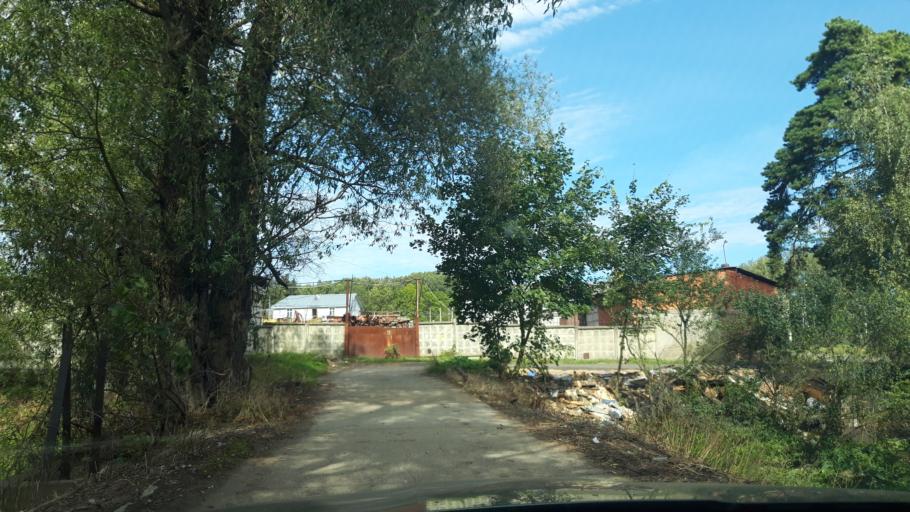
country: RU
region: Moskovskaya
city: Chashnikovo
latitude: 56.0327
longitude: 37.1706
